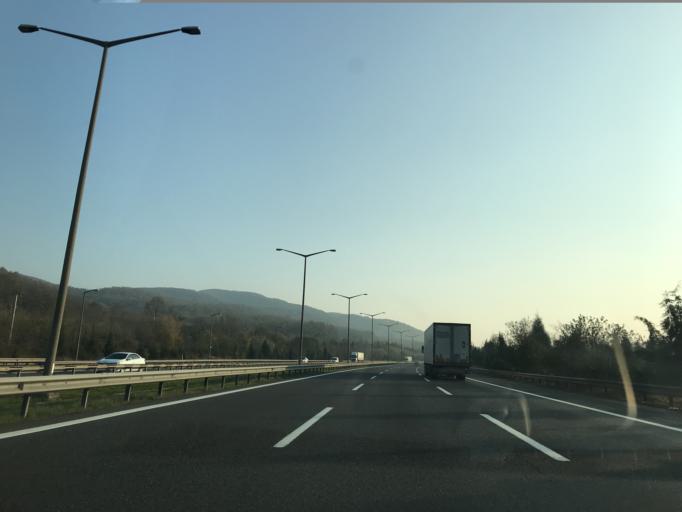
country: TR
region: Sakarya
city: Karadere
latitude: 40.8054
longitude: 30.8581
